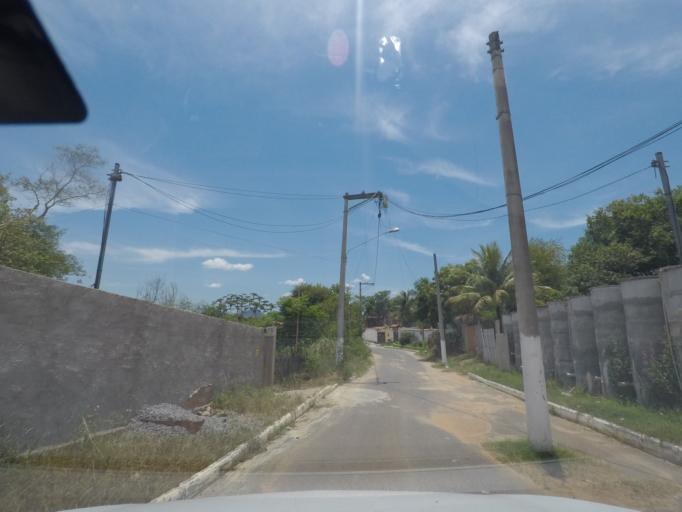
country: BR
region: Rio de Janeiro
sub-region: Marica
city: Marica
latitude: -22.9314
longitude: -42.8259
